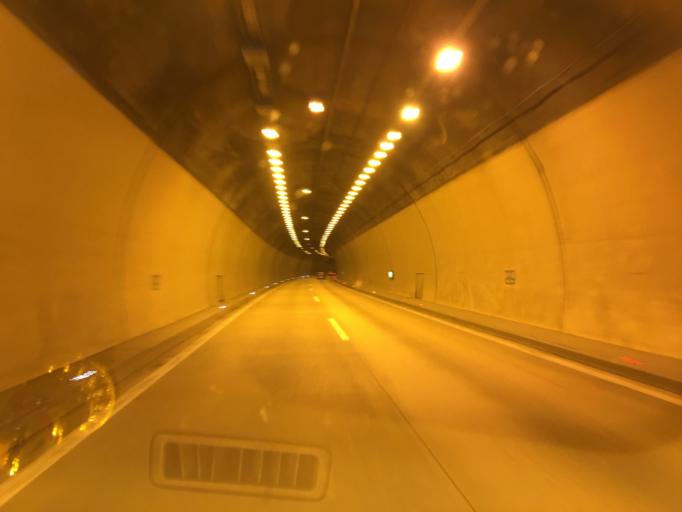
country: AT
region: Styria
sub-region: Politischer Bezirk Graz-Umgebung
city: Deutschfeistritz
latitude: 47.1917
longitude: 15.3283
